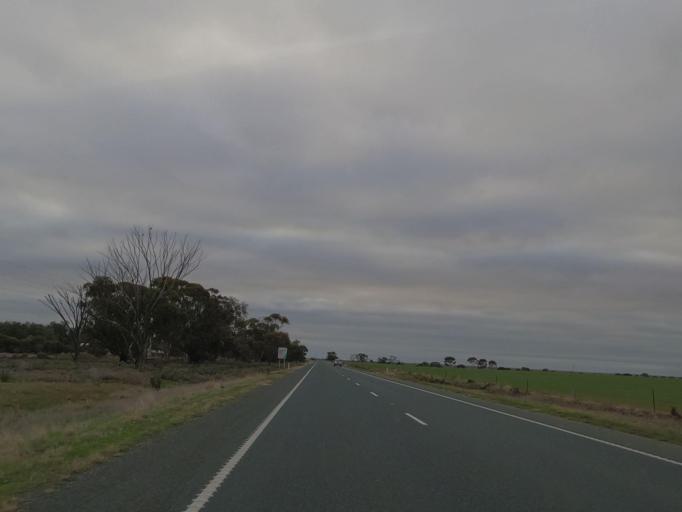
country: AU
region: Victoria
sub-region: Swan Hill
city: Swan Hill
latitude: -35.5601
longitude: 143.7807
